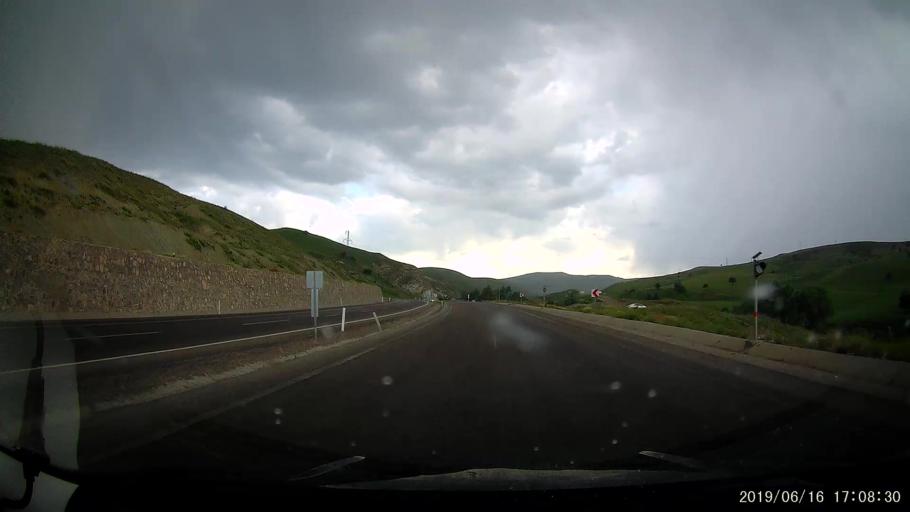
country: TR
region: Erzurum
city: Askale
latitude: 39.9081
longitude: 40.6603
